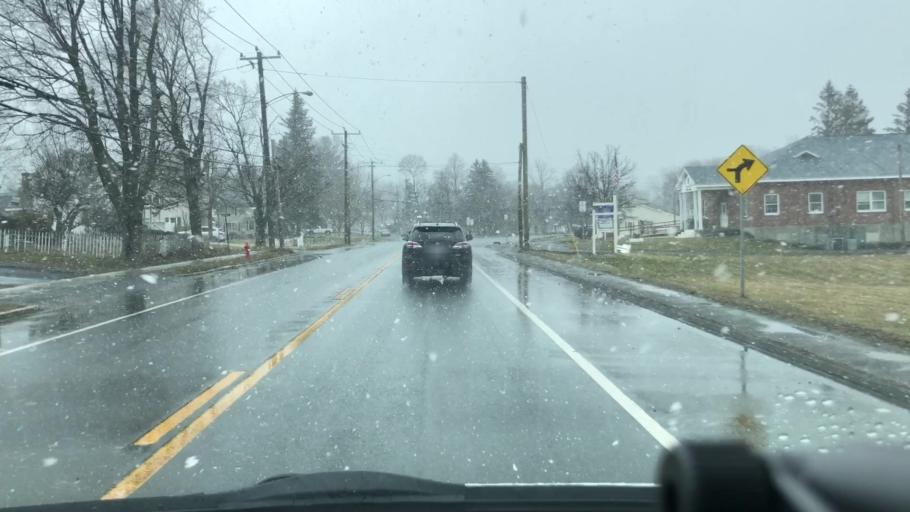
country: US
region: Massachusetts
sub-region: Berkshire County
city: Dalton
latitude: 42.4801
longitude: -73.1562
